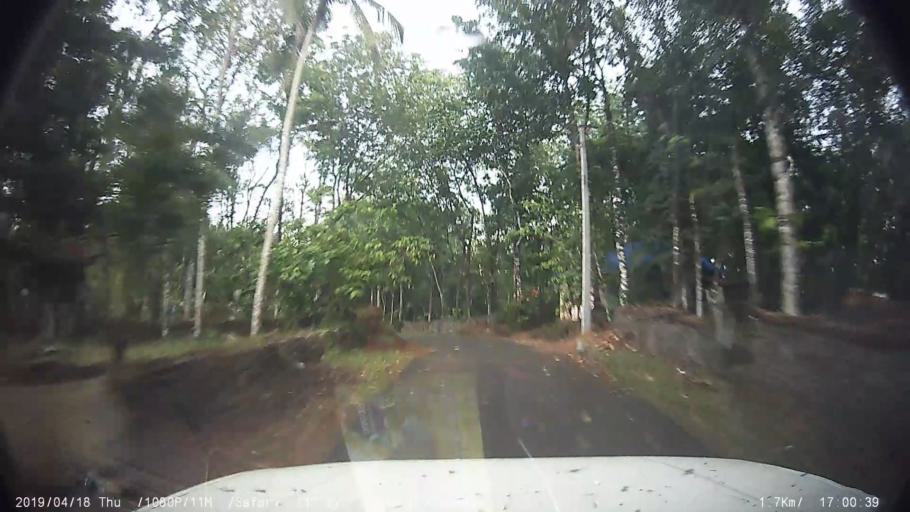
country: IN
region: Kerala
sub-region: Kottayam
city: Palackattumala
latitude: 9.7776
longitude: 76.5820
